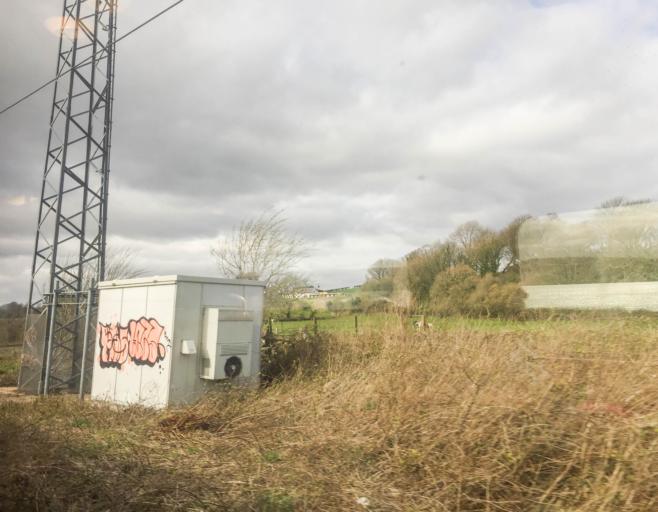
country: GB
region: Scotland
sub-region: Argyll and Bute
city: Cardross
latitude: 55.9526
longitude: -4.6312
